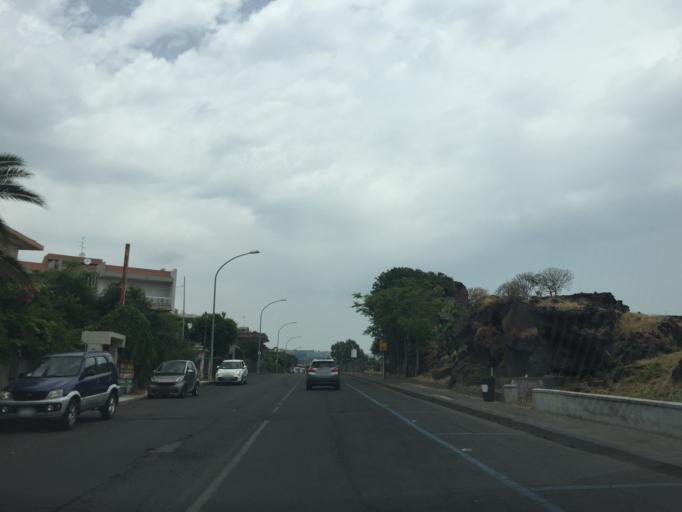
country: IT
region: Sicily
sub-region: Catania
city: Aci Castello
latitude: 37.5374
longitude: 15.1305
